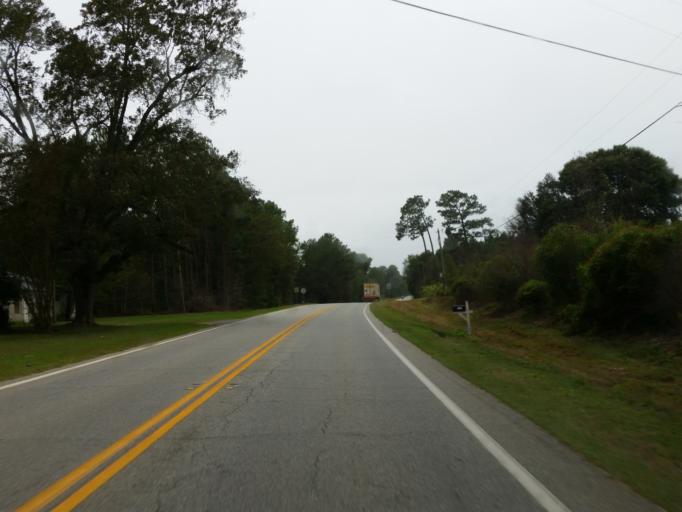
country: US
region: Georgia
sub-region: Berrien County
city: Ray City
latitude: 31.0739
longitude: -83.2110
